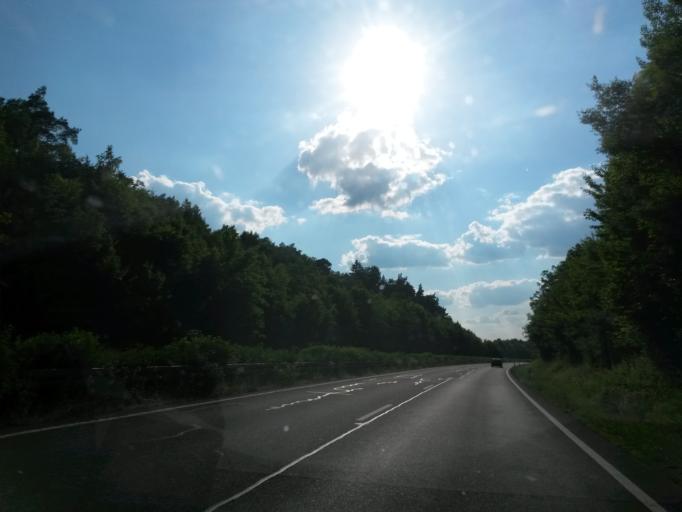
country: DE
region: Bavaria
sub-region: Regierungsbezirk Mittelfranken
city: Langenzenn
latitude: 49.4825
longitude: 10.7944
